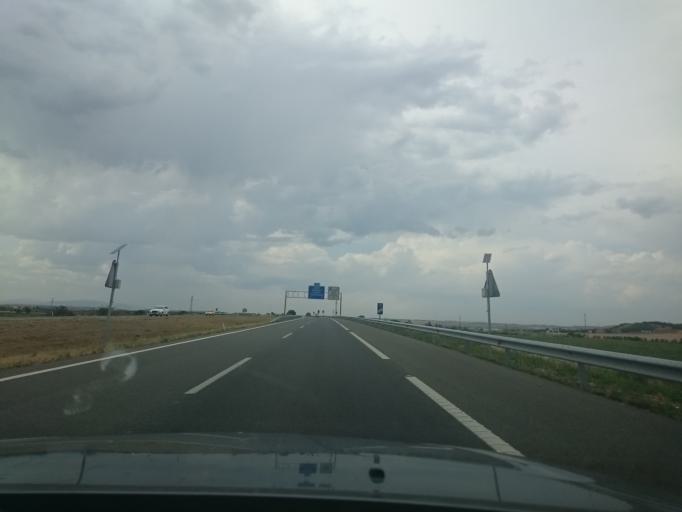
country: ES
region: Navarre
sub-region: Provincia de Navarra
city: Murchante
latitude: 42.0268
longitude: -1.6266
